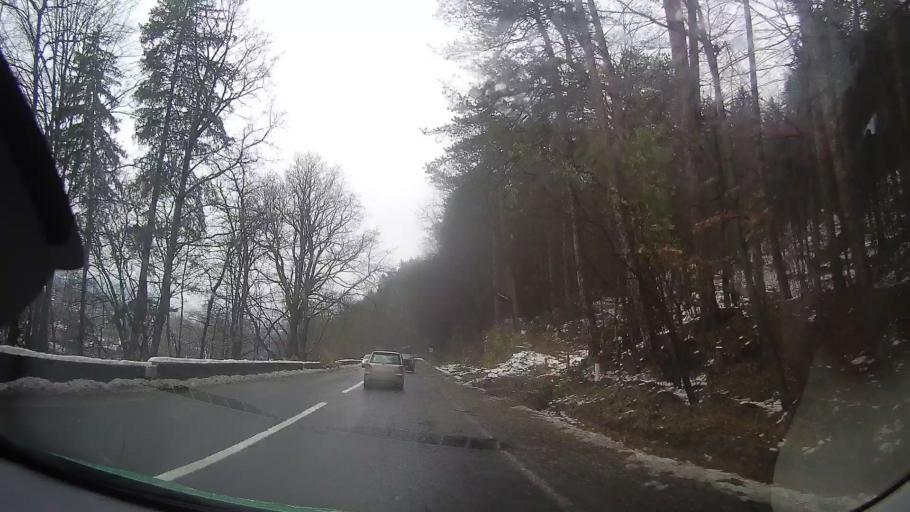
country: RO
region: Neamt
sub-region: Comuna Tarcau
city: Tarcau
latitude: 46.8964
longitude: 26.1224
